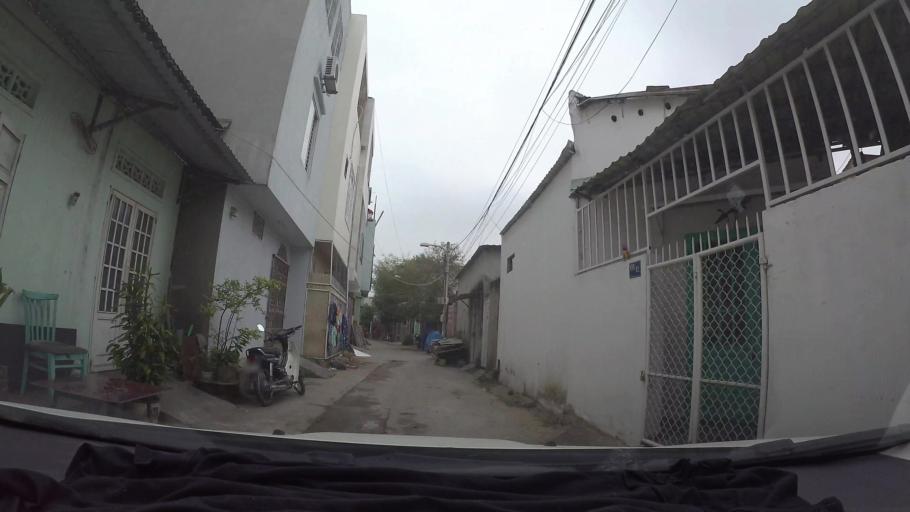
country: VN
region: Da Nang
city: Cam Le
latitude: 16.0247
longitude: 108.2103
